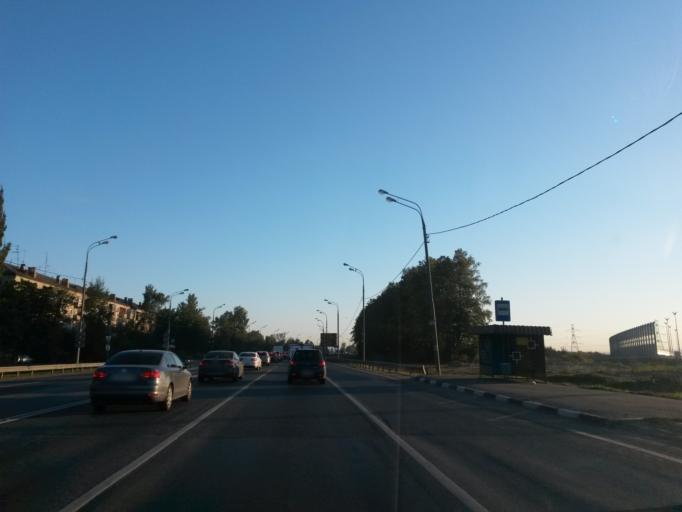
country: RU
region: Moskovskaya
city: Bolshevo
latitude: 55.9477
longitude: 37.8148
